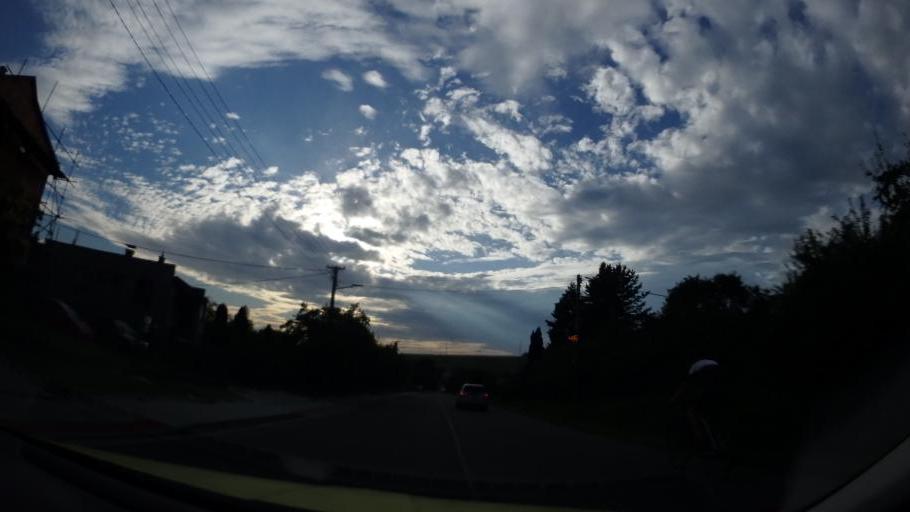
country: CZ
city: Rybi
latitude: 49.5988
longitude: 18.0846
